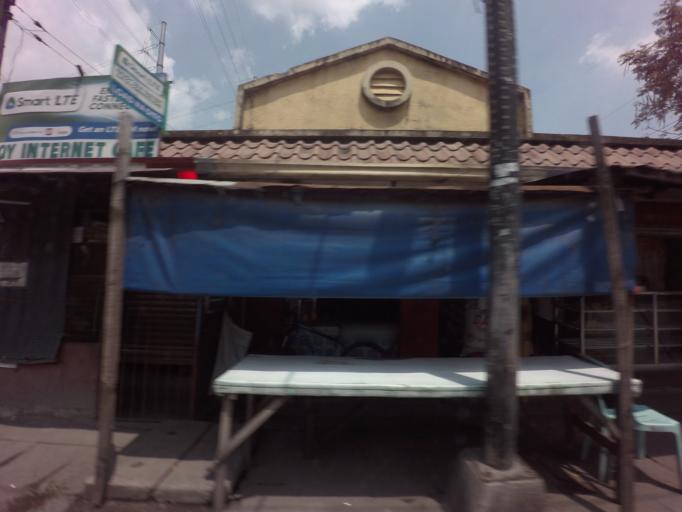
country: PH
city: Sambayanihan People's Village
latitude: 14.4446
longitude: 121.0505
